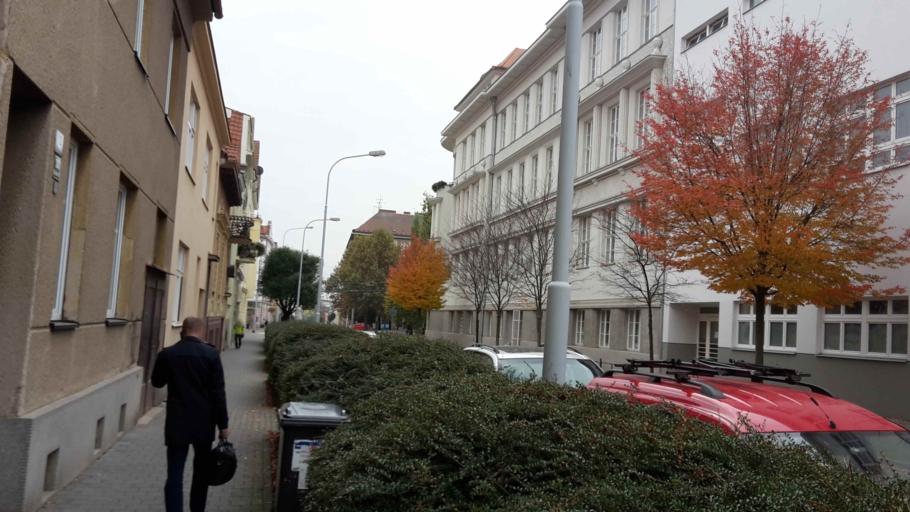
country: CZ
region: South Moravian
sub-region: Mesto Brno
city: Brno
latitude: 49.2246
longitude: 16.5920
